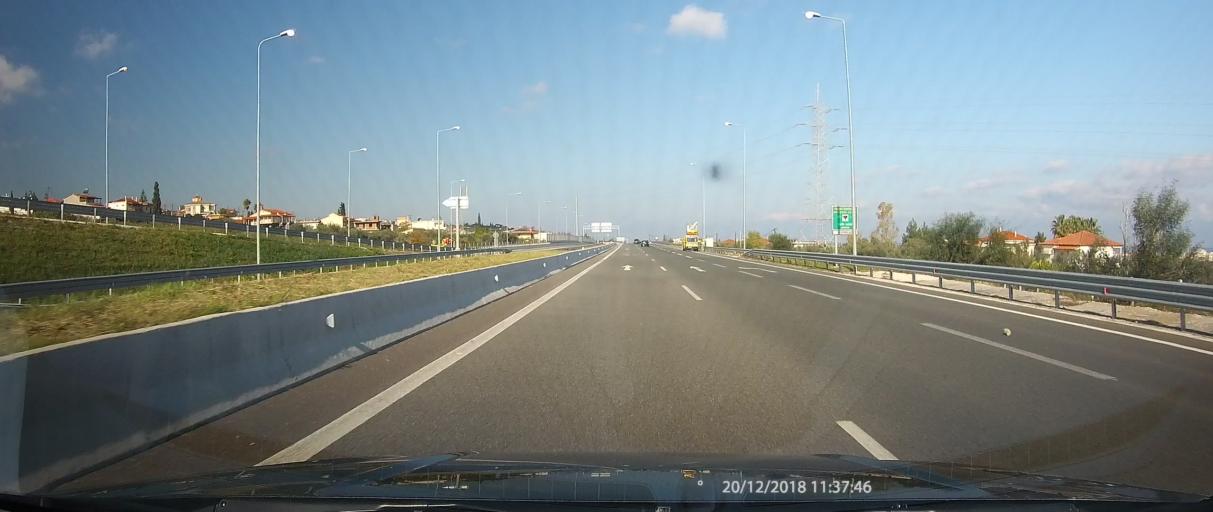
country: GR
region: Peloponnese
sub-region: Nomos Korinthias
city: Pasion
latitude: 38.0107
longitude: 22.7334
